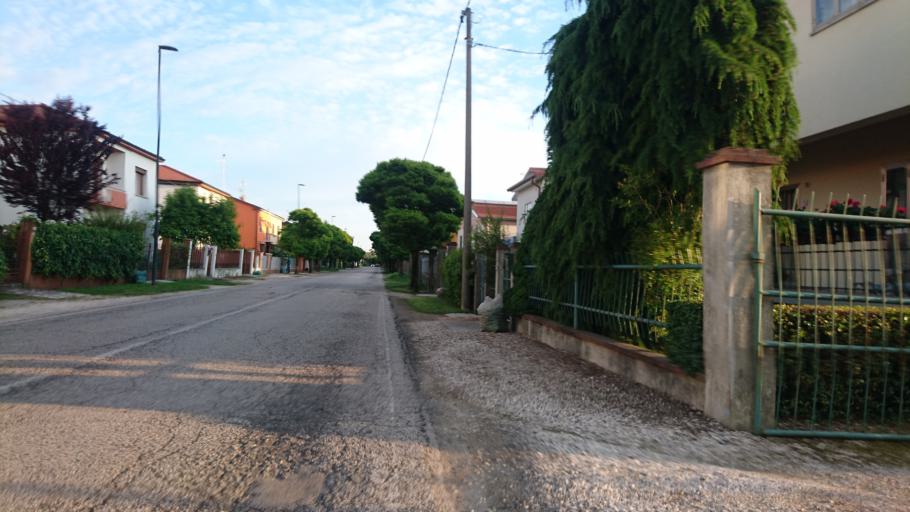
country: IT
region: Veneto
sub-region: Provincia di Rovigo
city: Castelmassa
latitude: 45.0211
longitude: 11.3162
